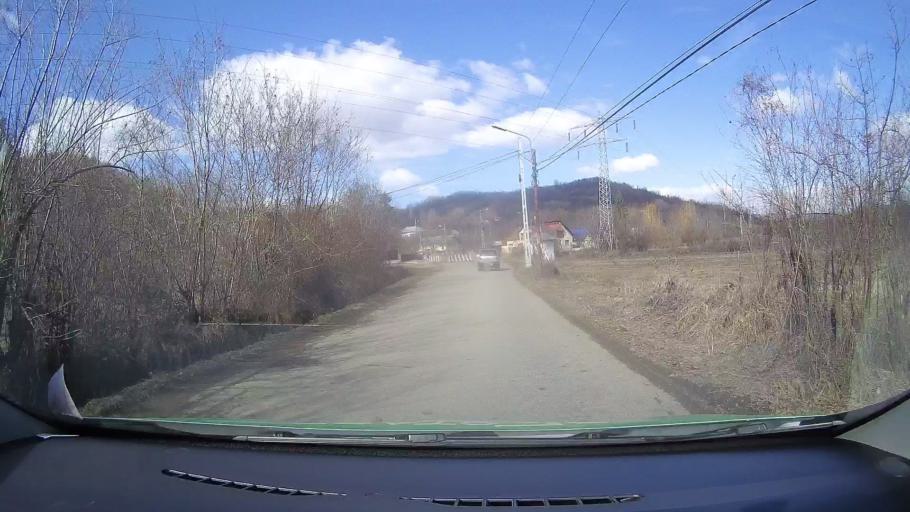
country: RO
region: Dambovita
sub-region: Oras Pucioasa
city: Pucioasa
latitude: 45.0677
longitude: 25.4240
